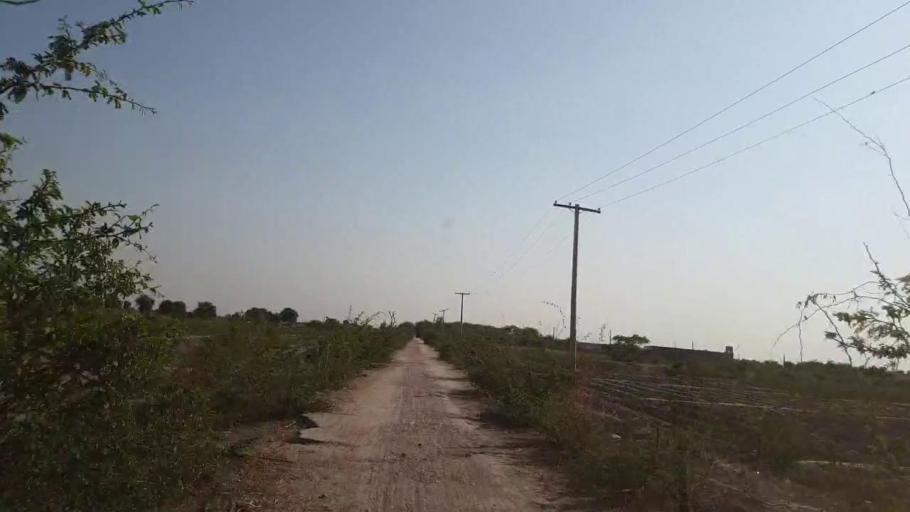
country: PK
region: Sindh
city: Naukot
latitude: 25.0228
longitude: 69.4696
